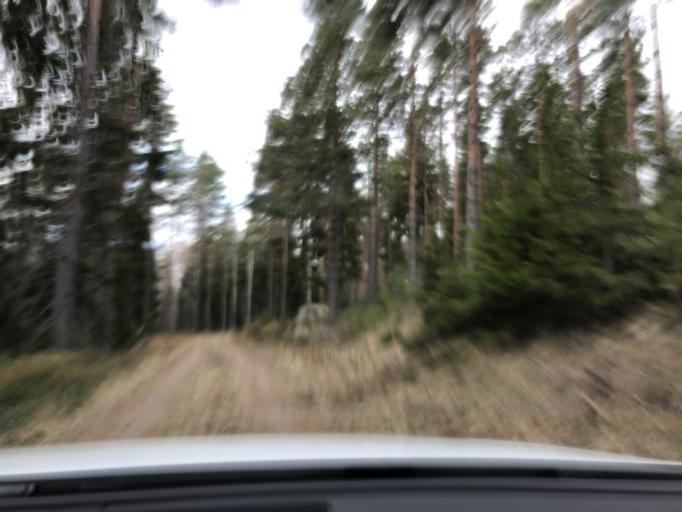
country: SE
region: Gaevleborg
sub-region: Gavle Kommun
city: Hedesunda
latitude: 60.3428
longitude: 17.0641
